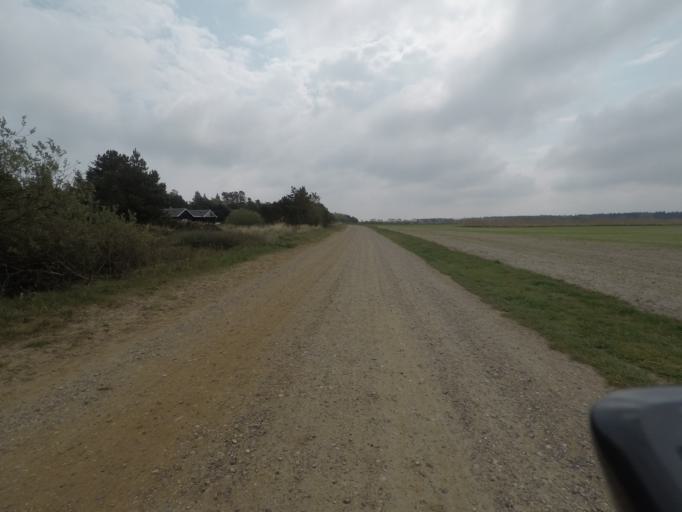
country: DE
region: Schleswig-Holstein
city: List
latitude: 55.0899
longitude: 8.5224
